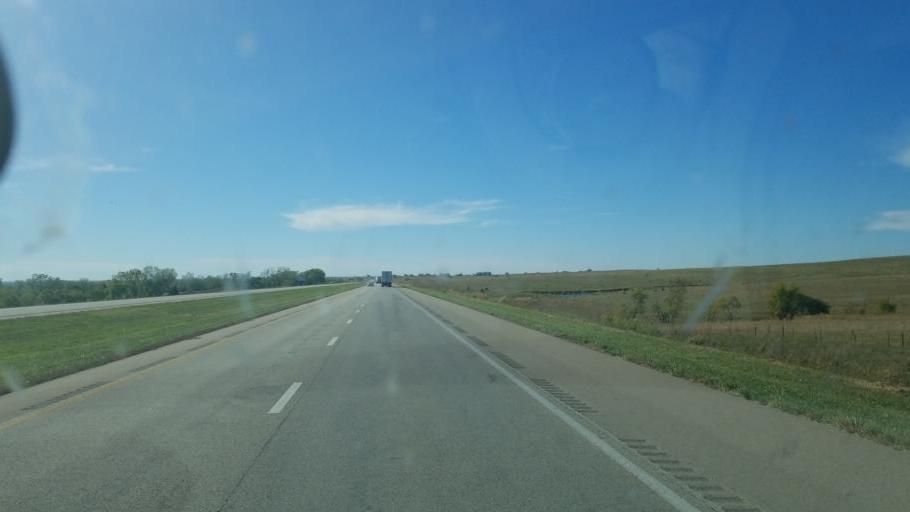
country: US
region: Kansas
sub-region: Saline County
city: Salina
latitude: 38.8783
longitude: -97.6883
